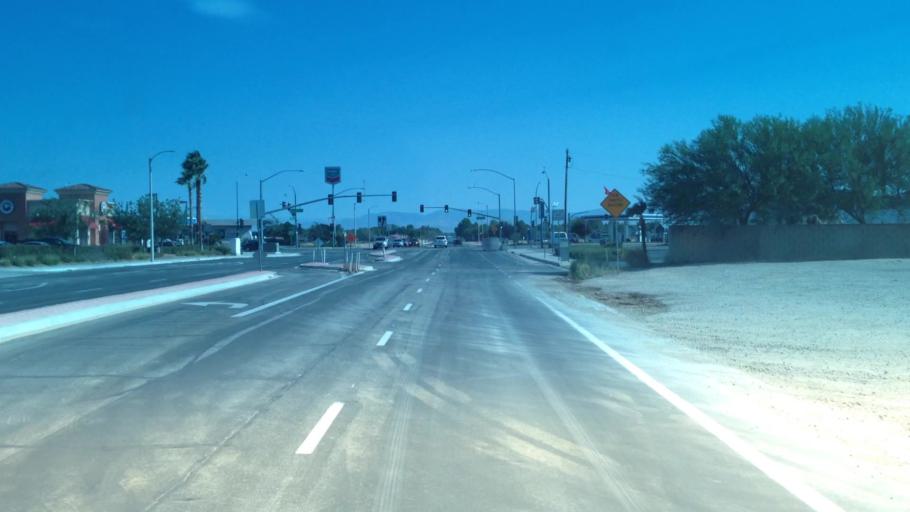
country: US
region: California
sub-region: Los Angeles County
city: Lancaster
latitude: 34.7054
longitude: -118.1661
